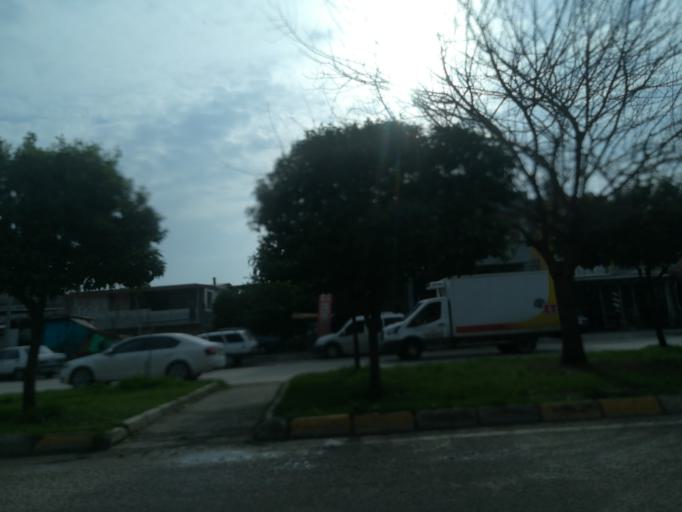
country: TR
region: Adana
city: Adana
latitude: 37.0026
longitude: 35.3551
